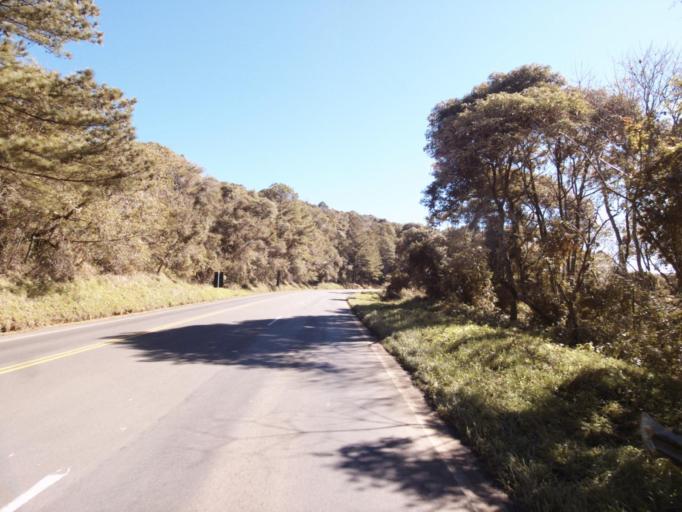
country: BR
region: Santa Catarina
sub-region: Joacaba
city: Joacaba
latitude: -26.9816
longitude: -51.7551
